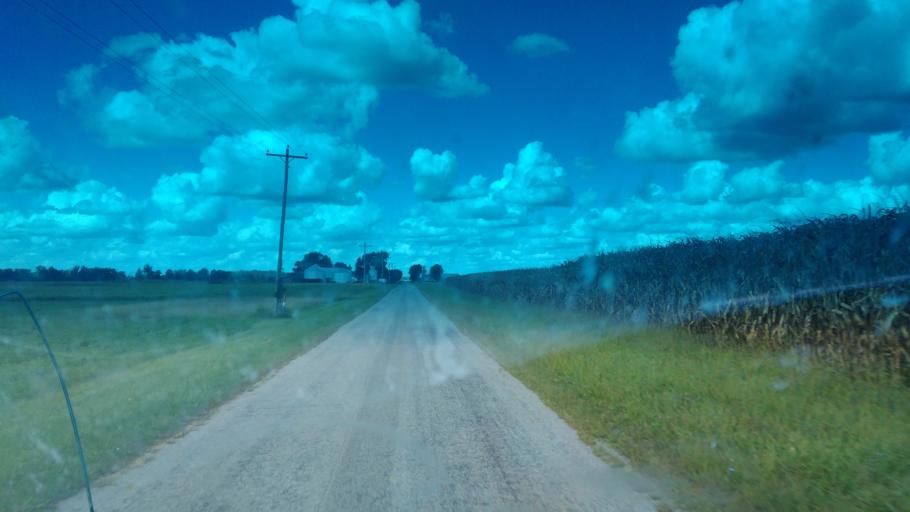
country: US
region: Ohio
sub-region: Union County
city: Richwood
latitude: 40.4472
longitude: -83.4932
